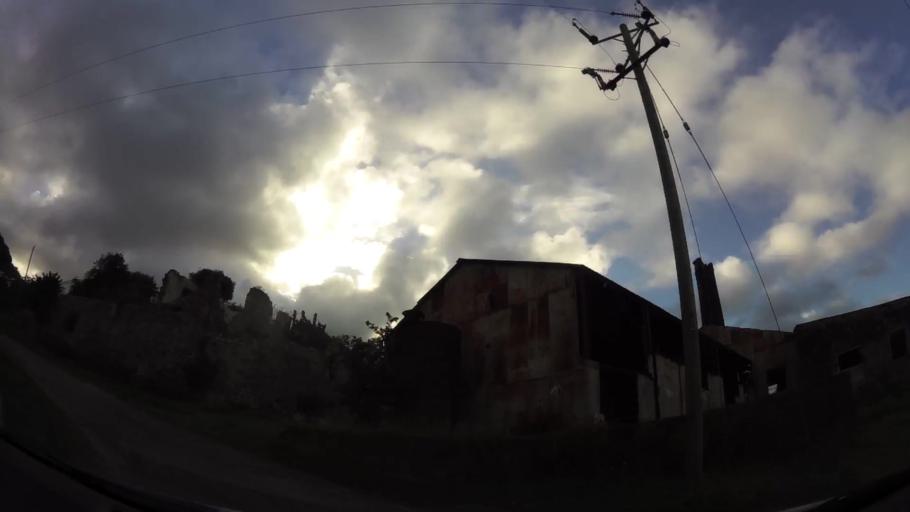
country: KN
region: Saint Mary Cayon
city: Cayon
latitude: 17.3489
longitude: -62.7308
